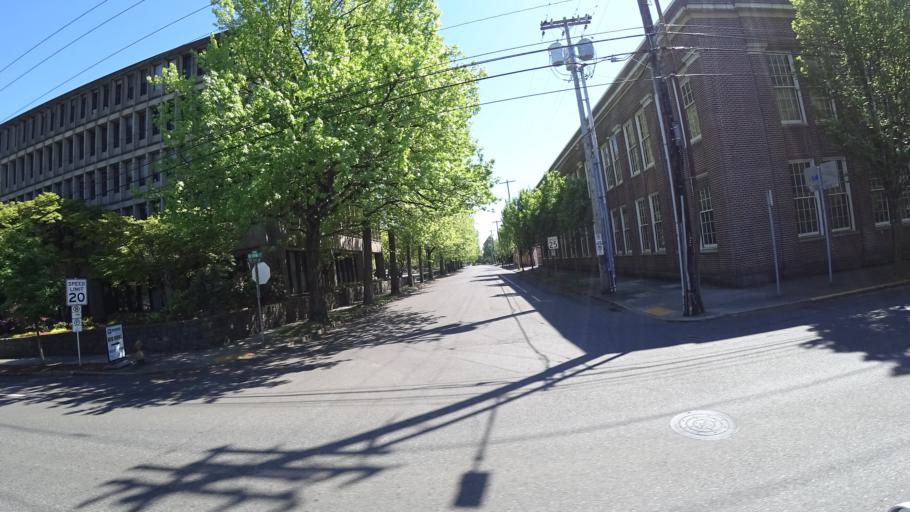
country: US
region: Oregon
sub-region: Multnomah County
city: Portland
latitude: 45.5280
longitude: -122.6504
